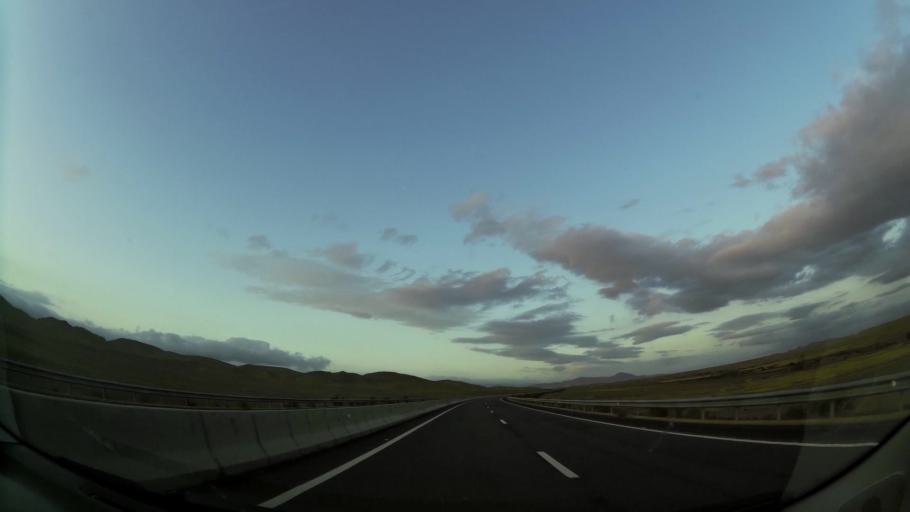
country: MA
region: Oriental
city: Taourirt
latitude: 34.5845
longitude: -2.8025
